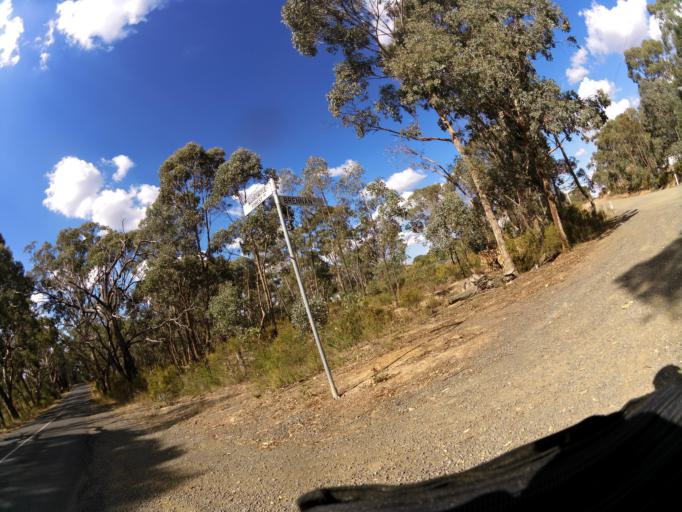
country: AU
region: Victoria
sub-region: Greater Bendigo
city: Kennington
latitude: -36.9524
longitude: 144.7757
